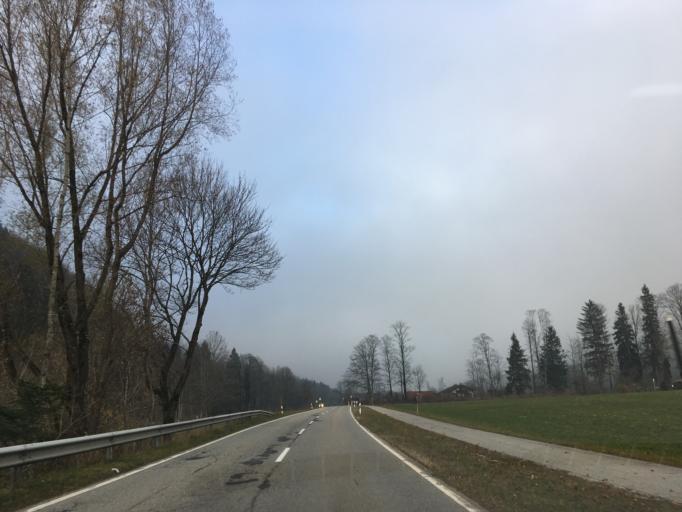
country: AT
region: Tyrol
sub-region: Politischer Bezirk Kufstein
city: Rettenschoss
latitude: 47.6981
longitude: 12.2713
